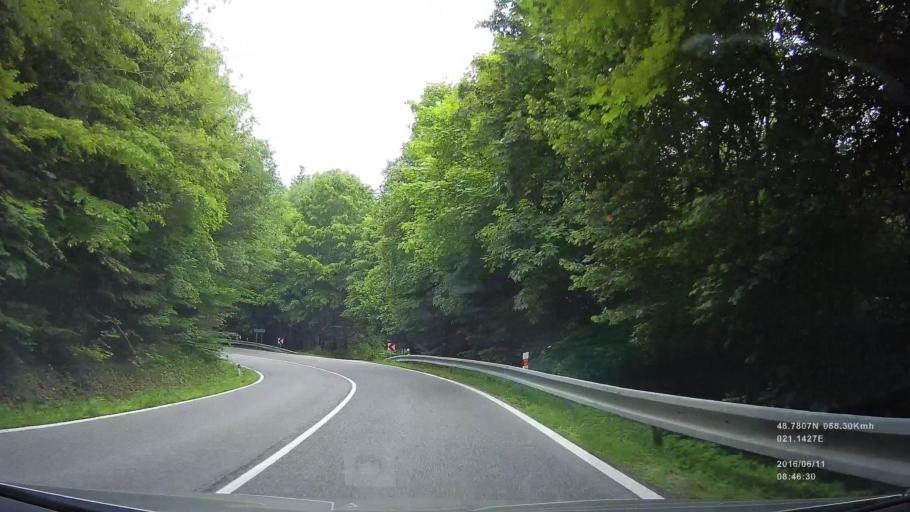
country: SK
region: Kosicky
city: Kosice
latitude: 48.7599
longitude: 21.1803
